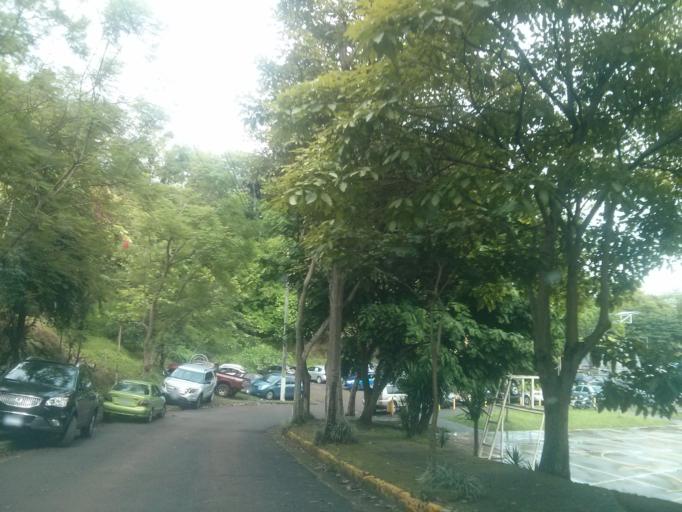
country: CR
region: San Jose
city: Calle Blancos
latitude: 9.9395
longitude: -84.0688
